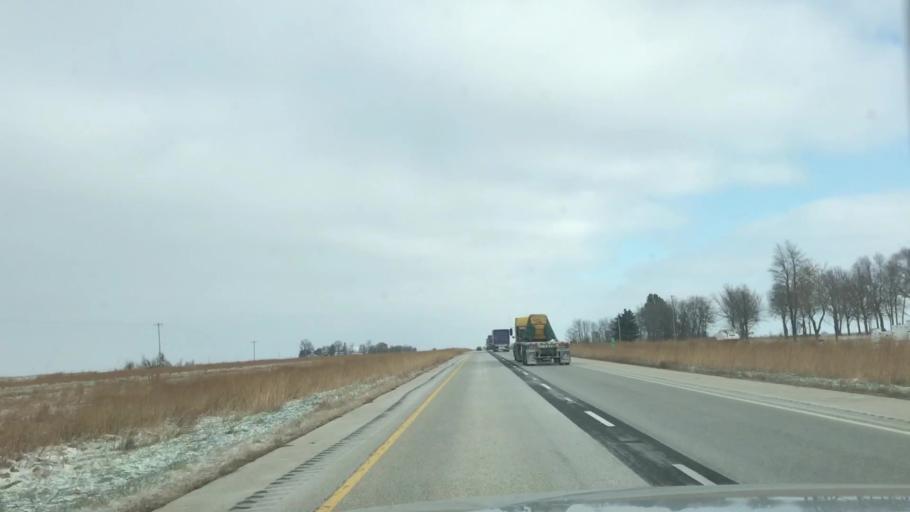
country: US
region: Illinois
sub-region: Sangamon County
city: Divernon
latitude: 39.5074
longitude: -89.6453
